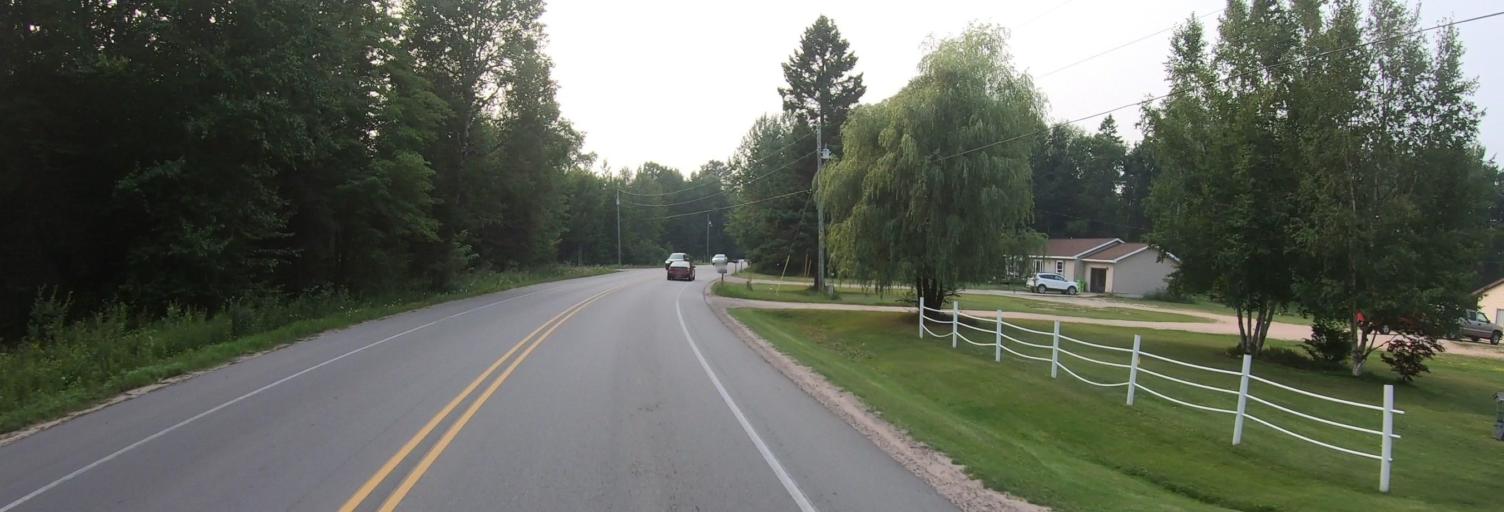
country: US
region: Michigan
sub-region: Chippewa County
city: Sault Ste. Marie
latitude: 46.4544
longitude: -84.6106
